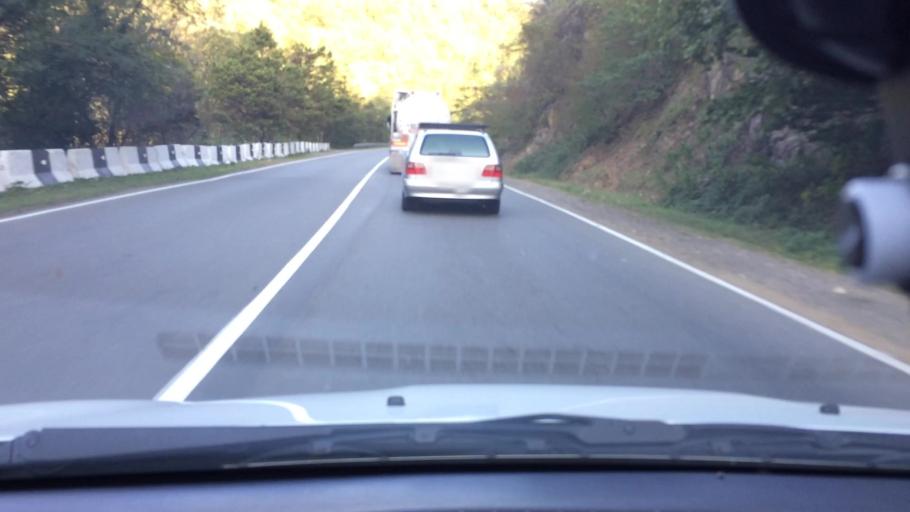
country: GE
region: Imereti
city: Kharagauli
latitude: 42.1070
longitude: 43.2046
